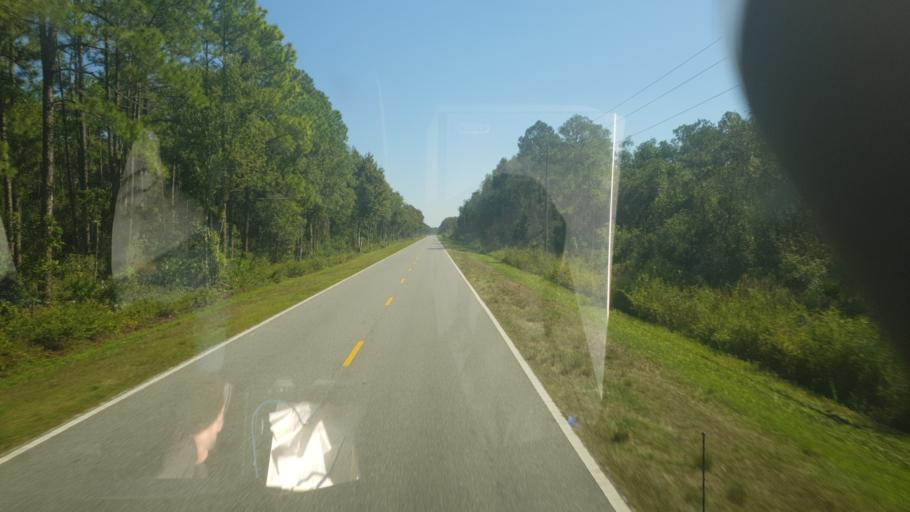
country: US
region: Florida
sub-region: Lake County
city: Four Corners
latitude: 28.3761
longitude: -81.7777
